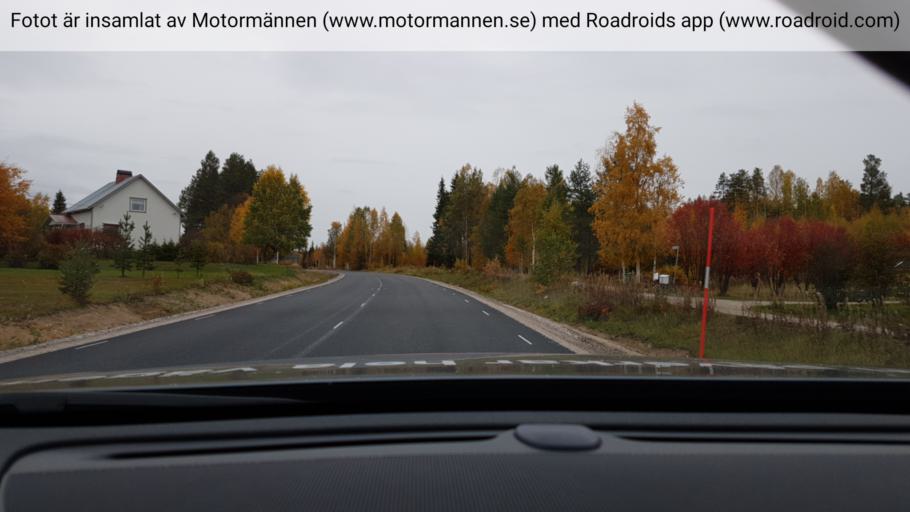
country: SE
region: Norrbotten
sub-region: Overkalix Kommun
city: OEverkalix
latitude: 66.3679
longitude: 22.8431
